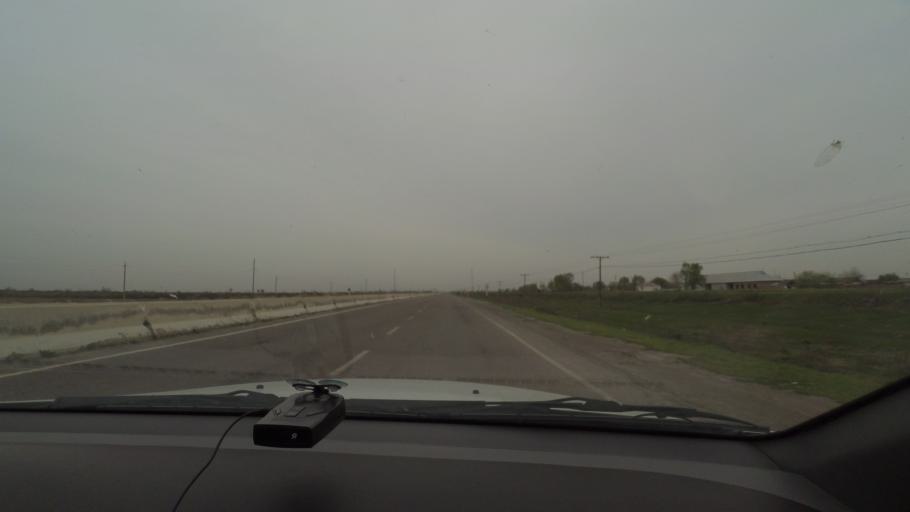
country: UZ
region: Sirdaryo
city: Guliston
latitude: 40.4944
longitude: 68.6530
